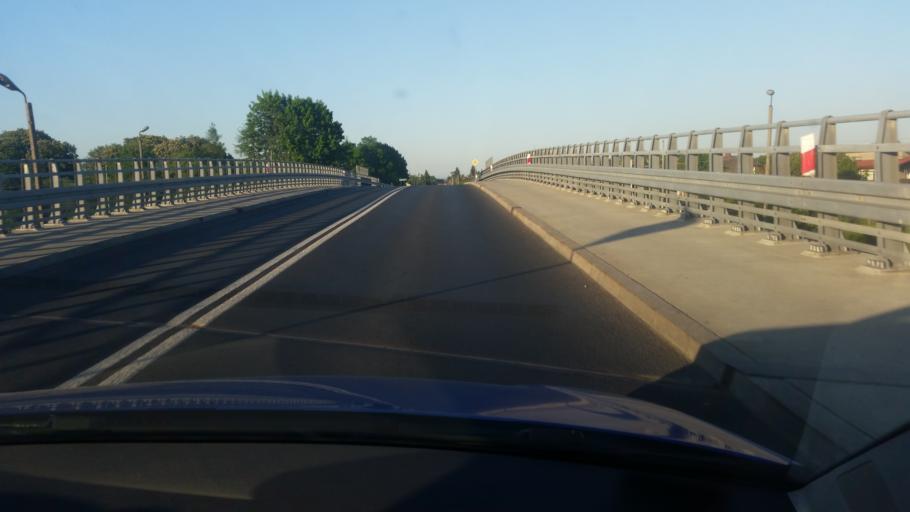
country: PL
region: Silesian Voivodeship
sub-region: Powiat czestochowski
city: Klomnice
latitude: 50.9182
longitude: 19.3412
